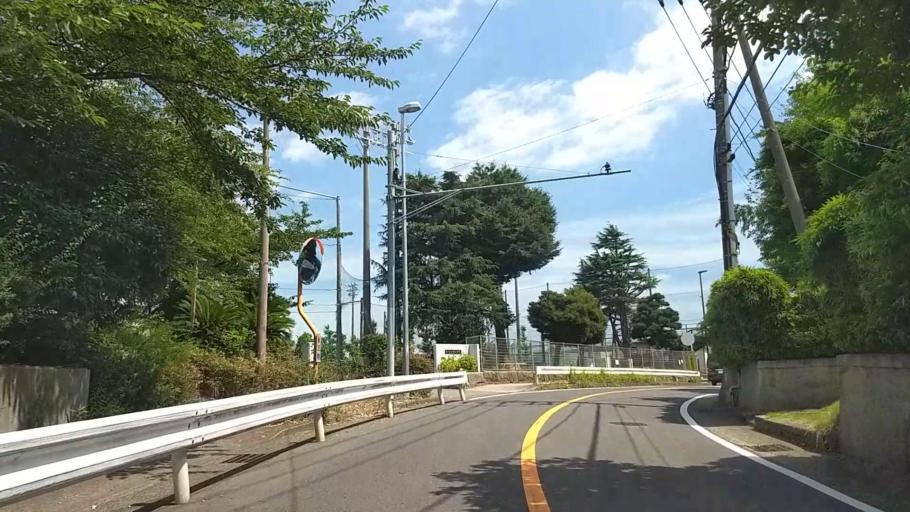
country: JP
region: Kanagawa
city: Fujisawa
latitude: 35.3497
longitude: 139.4588
